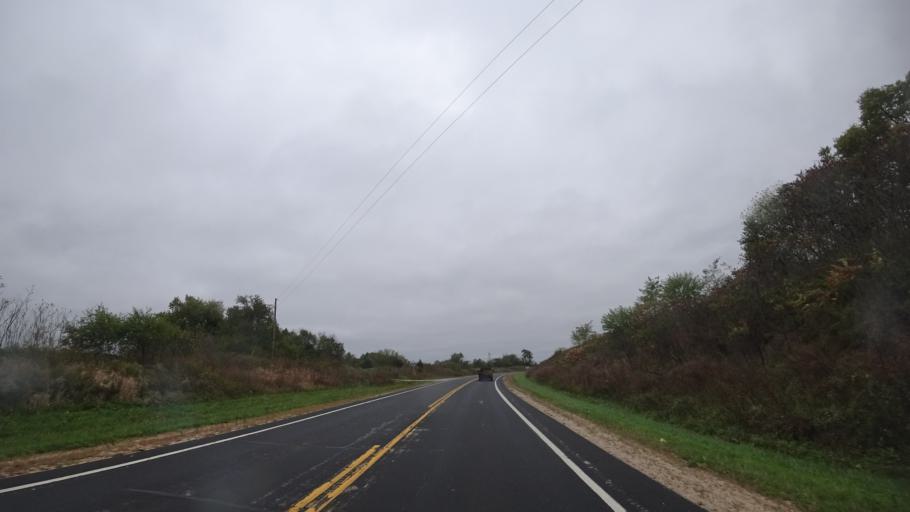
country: US
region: Wisconsin
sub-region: Grant County
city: Boscobel
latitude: 43.1137
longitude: -90.7942
